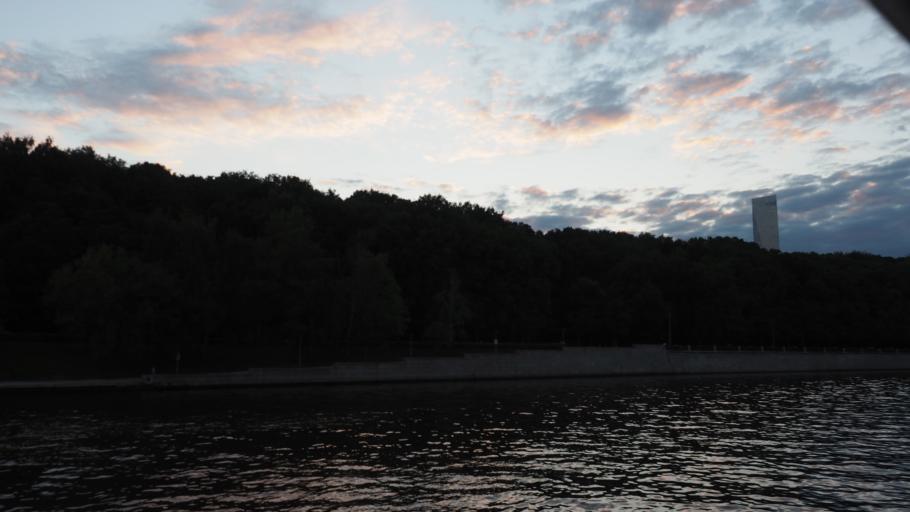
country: RU
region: Moscow
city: Vorob'yovo
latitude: 55.7153
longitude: 37.5426
